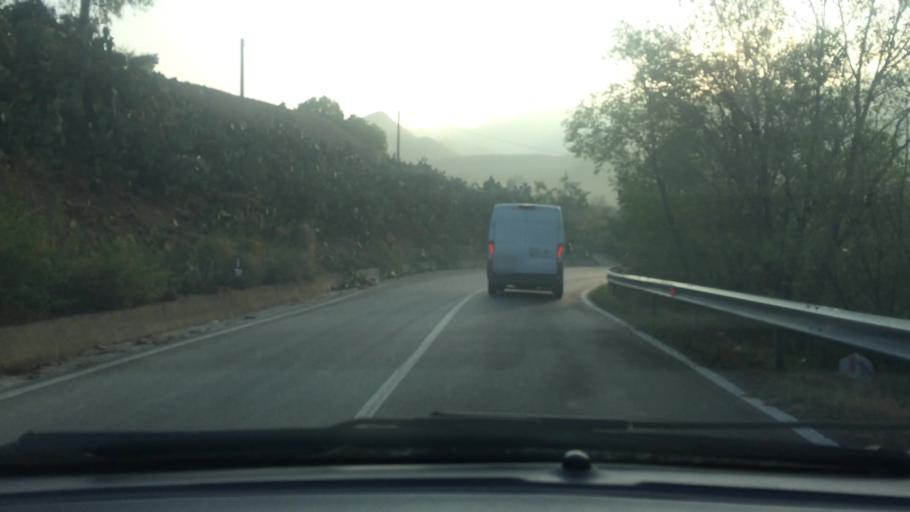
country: IT
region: Basilicate
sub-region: Provincia di Matera
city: Montescaglioso
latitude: 40.5356
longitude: 16.6433
